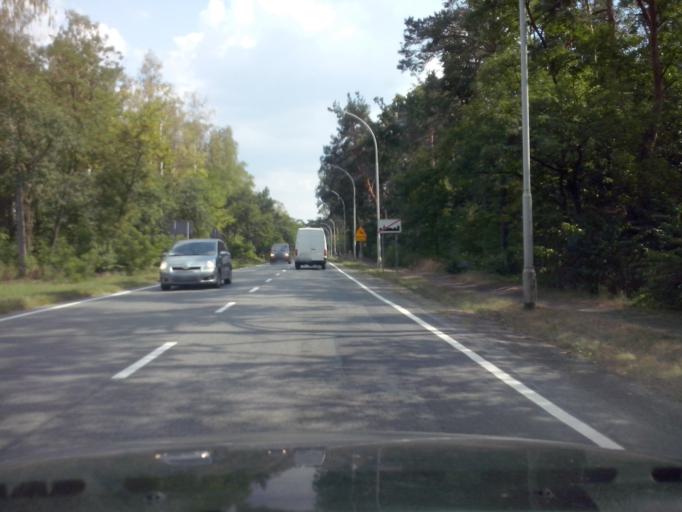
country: PL
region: Subcarpathian Voivodeship
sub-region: Powiat nizanski
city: Rudnik nad Sanem
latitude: 50.4372
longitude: 22.2609
